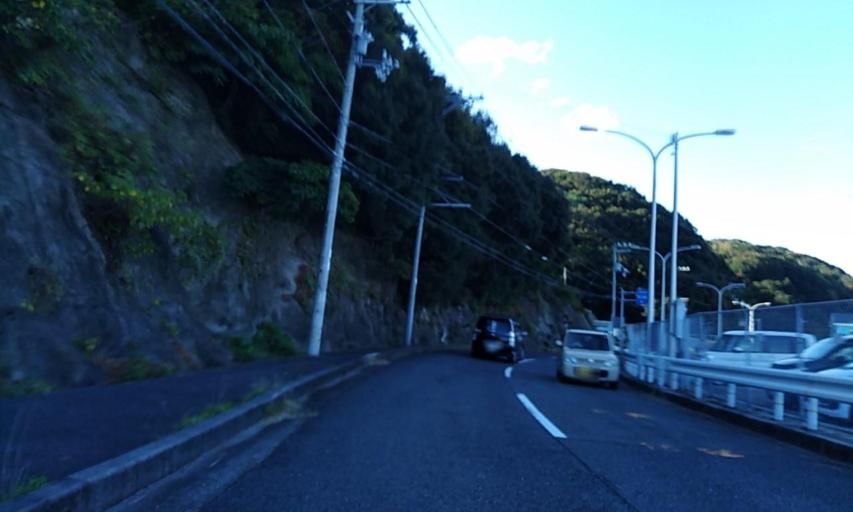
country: JP
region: Wakayama
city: Minato
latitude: 34.3127
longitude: 135.0943
